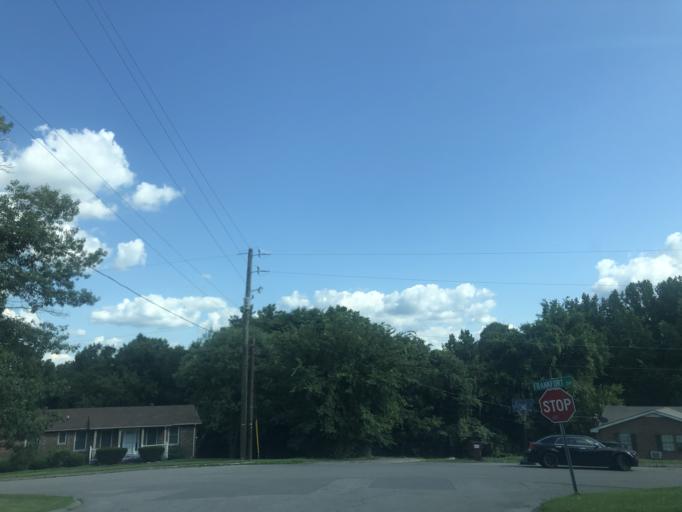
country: US
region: Tennessee
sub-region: Wilson County
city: Green Hill
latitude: 36.2058
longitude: -86.5926
